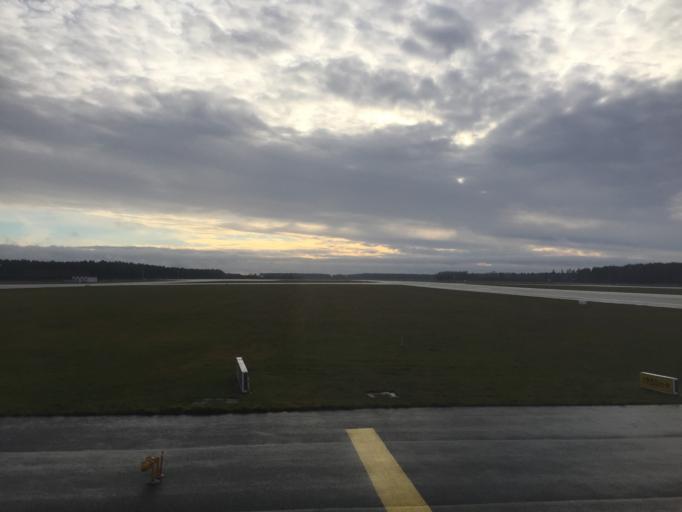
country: LV
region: Babite
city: Pinki
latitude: 56.9172
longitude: 23.9716
